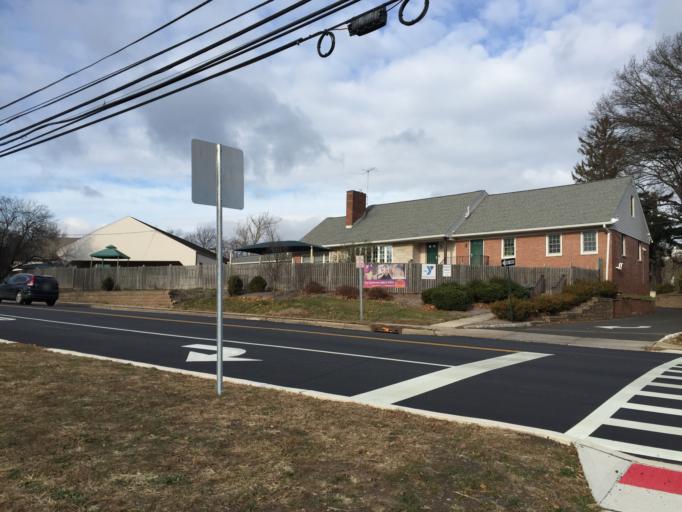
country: US
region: New Jersey
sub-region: Union County
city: Springfield
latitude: 40.7118
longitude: -74.3451
